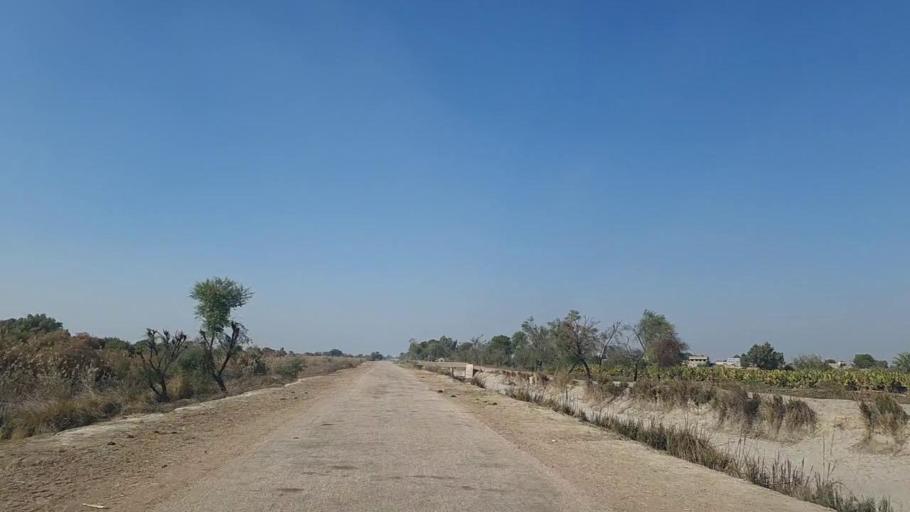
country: PK
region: Sindh
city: Jam Sahib
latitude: 26.2200
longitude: 68.6035
